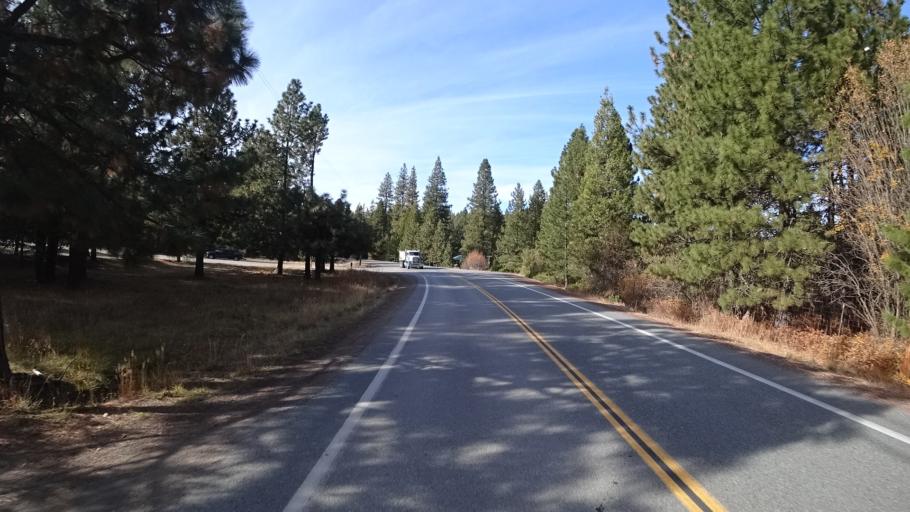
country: US
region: California
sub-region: Siskiyou County
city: Weed
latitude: 41.3828
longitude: -122.3967
